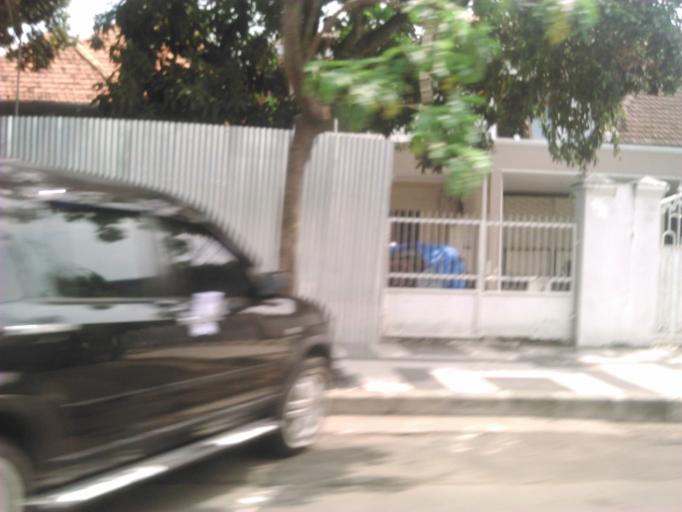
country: ID
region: East Java
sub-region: Kota Surabaya
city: Surabaya
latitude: -7.2587
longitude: 112.7479
